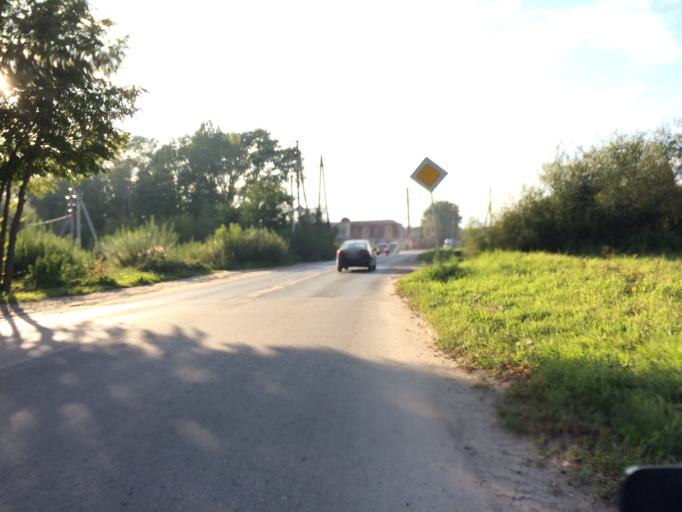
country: RU
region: Mariy-El
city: Yoshkar-Ola
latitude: 56.6501
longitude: 47.9607
